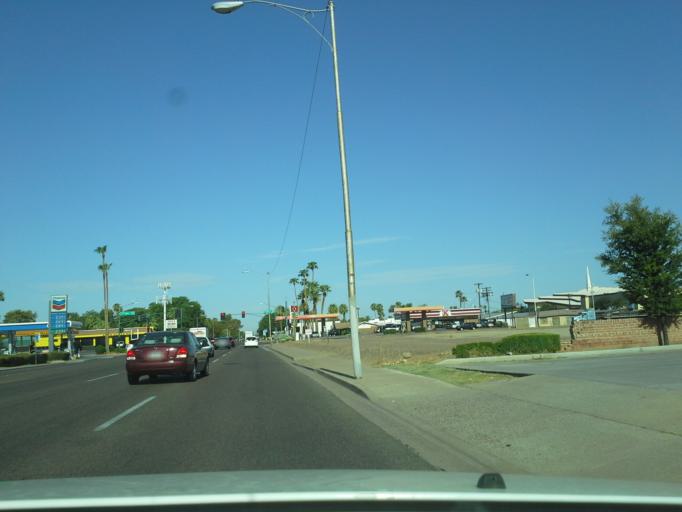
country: US
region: Arizona
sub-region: Maricopa County
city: Phoenix
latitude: 33.5239
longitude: -112.0809
